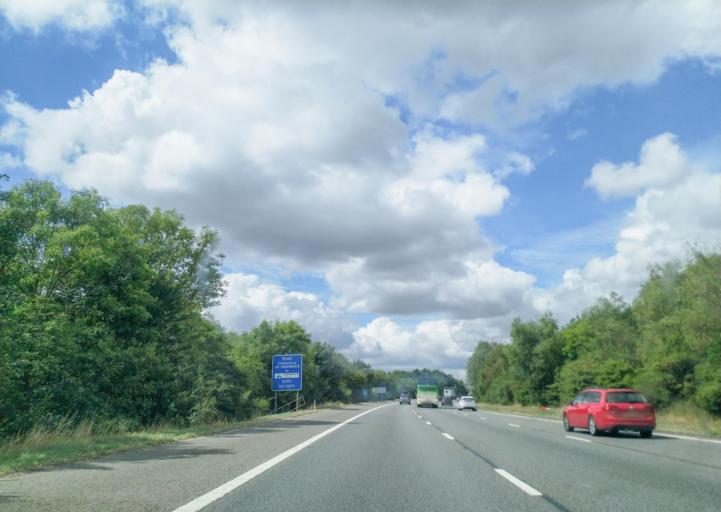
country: GB
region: England
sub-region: Warwickshire
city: Warwick
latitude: 52.2567
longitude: -1.5996
